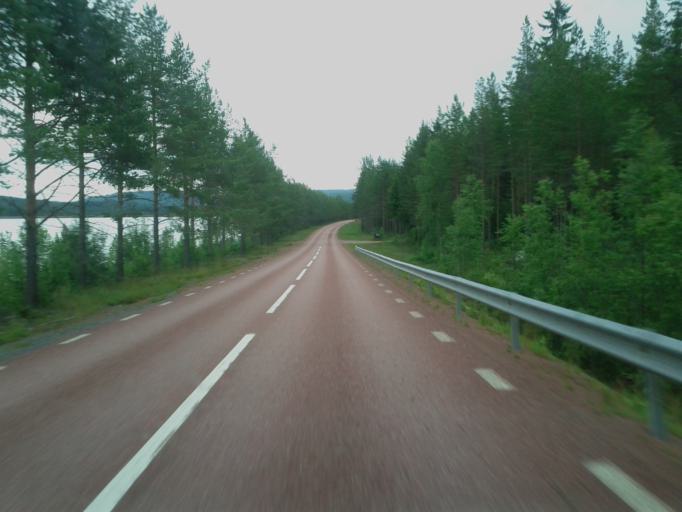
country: SE
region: Dalarna
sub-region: Alvdalens Kommun
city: AElvdalen
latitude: 61.2903
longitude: 13.7419
